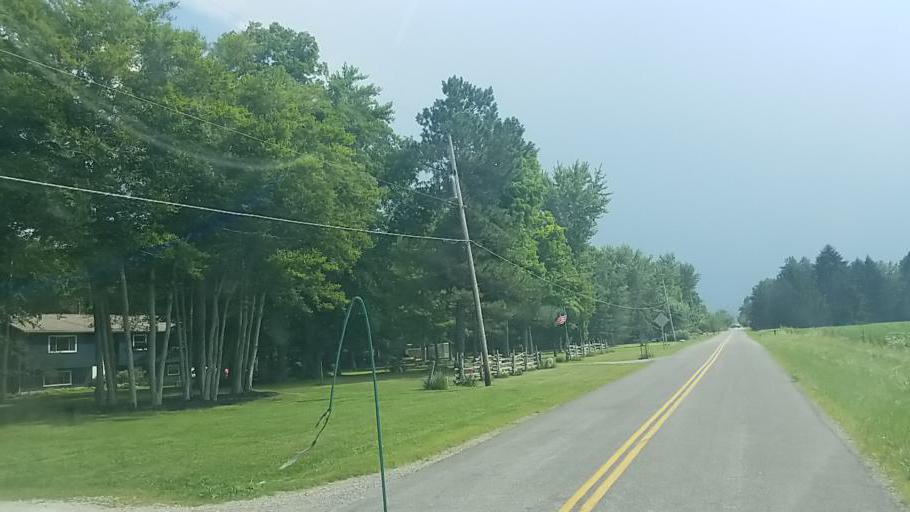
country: US
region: Ohio
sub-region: Medina County
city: Westfield Center
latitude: 41.1049
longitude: -81.9622
